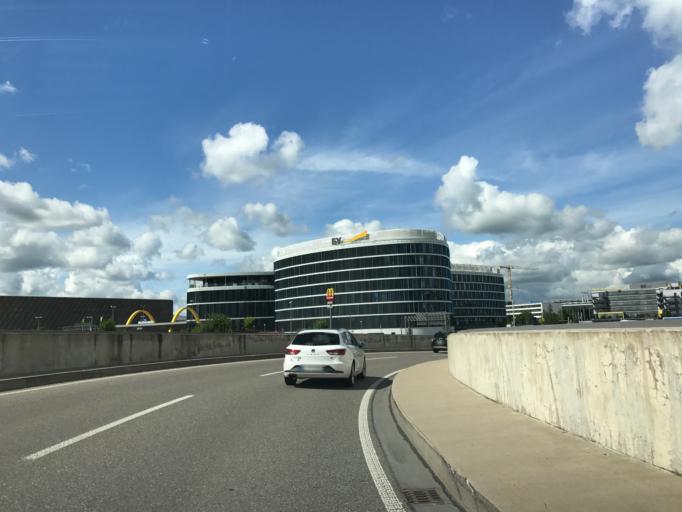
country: DE
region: Baden-Wuerttemberg
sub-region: Regierungsbezirk Stuttgart
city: Leinfelden-Echterdingen
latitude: 48.6947
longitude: 9.1985
